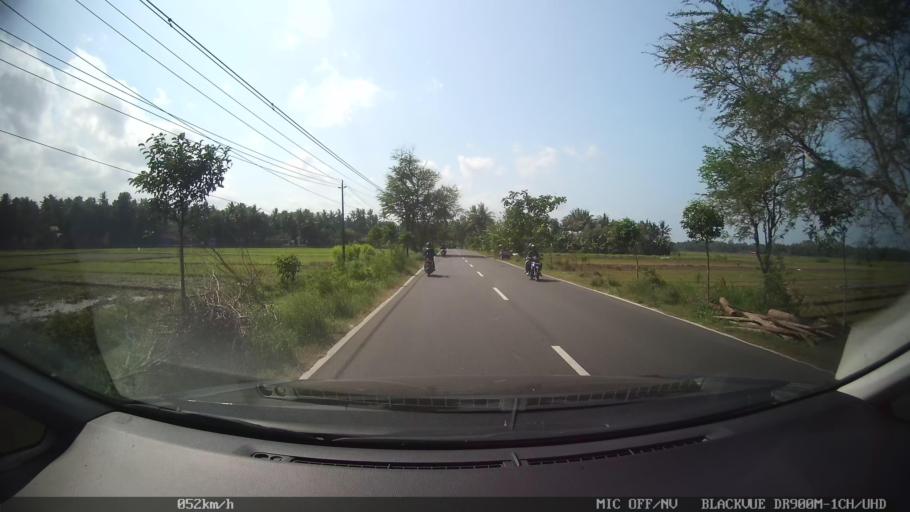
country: ID
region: Daerah Istimewa Yogyakarta
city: Srandakan
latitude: -7.9328
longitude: 110.2146
